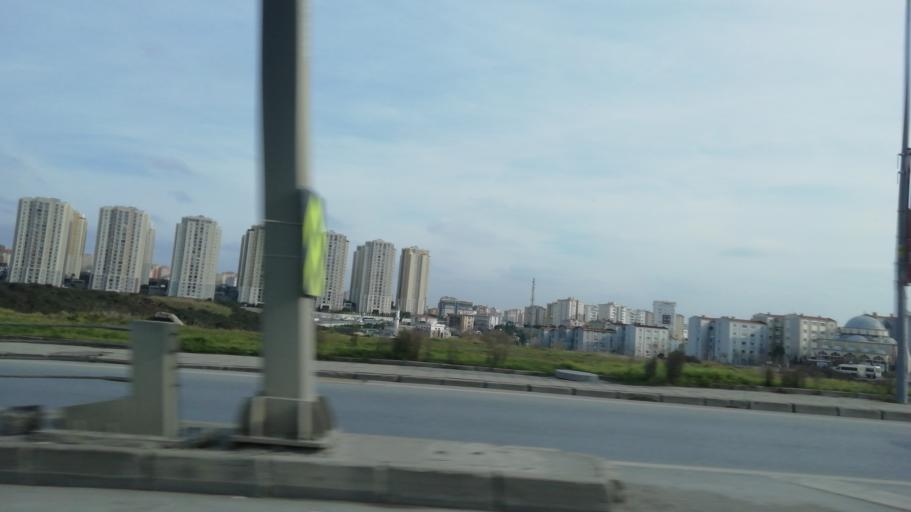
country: TR
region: Istanbul
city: Basaksehir
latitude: 41.1053
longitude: 28.7946
